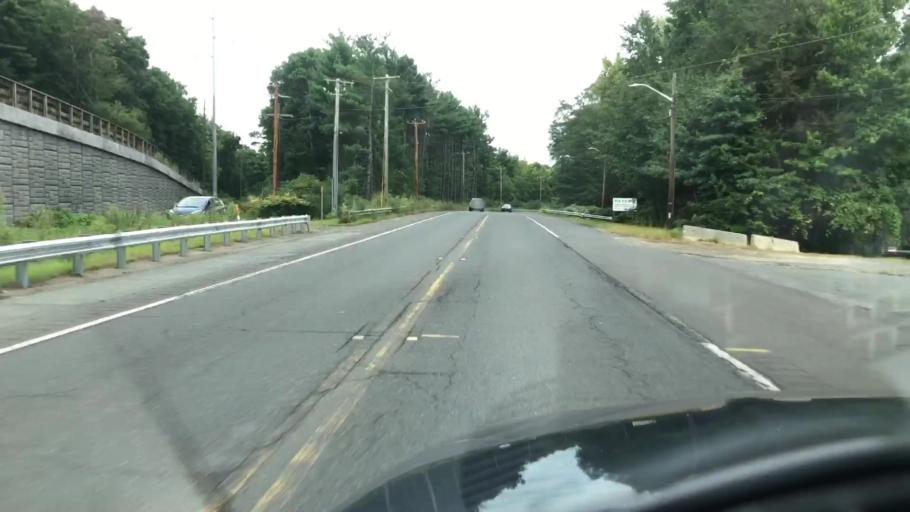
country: US
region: Massachusetts
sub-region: Hampshire County
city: Northampton
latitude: 42.3003
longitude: -72.6560
